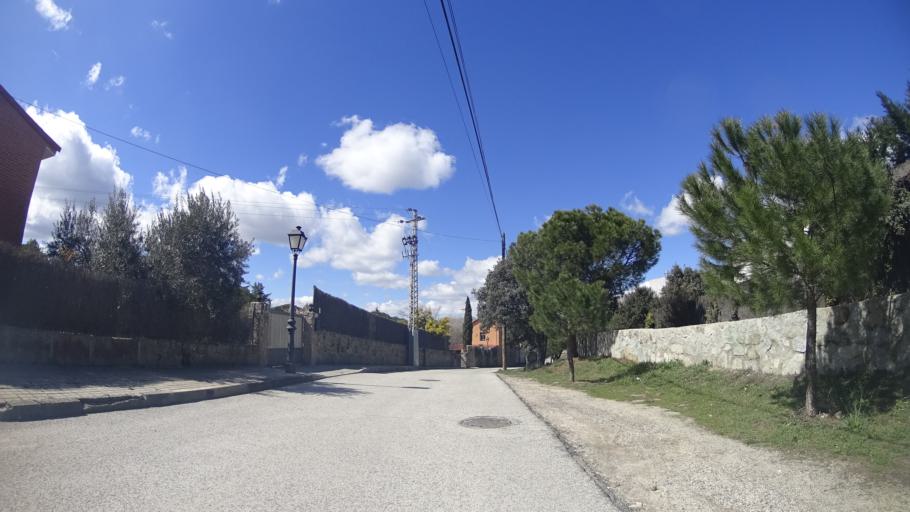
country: ES
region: Madrid
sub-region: Provincia de Madrid
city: Torrelodones
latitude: 40.5705
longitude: -3.9499
